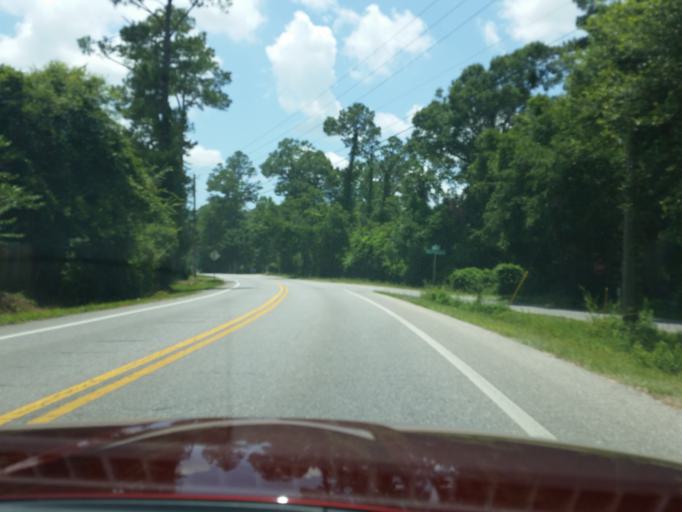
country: US
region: Florida
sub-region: Escambia County
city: Gonzalez
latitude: 30.5821
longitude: -87.2908
